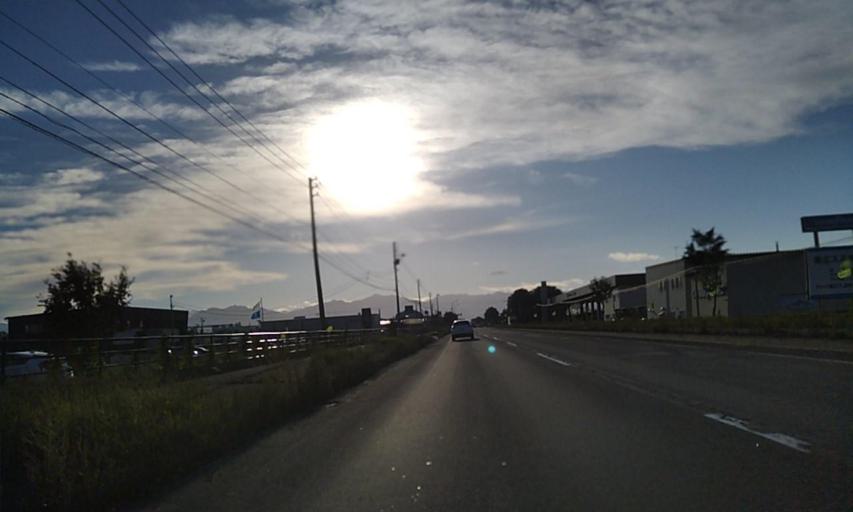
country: JP
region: Hokkaido
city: Obihiro
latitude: 42.9251
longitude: 143.1063
